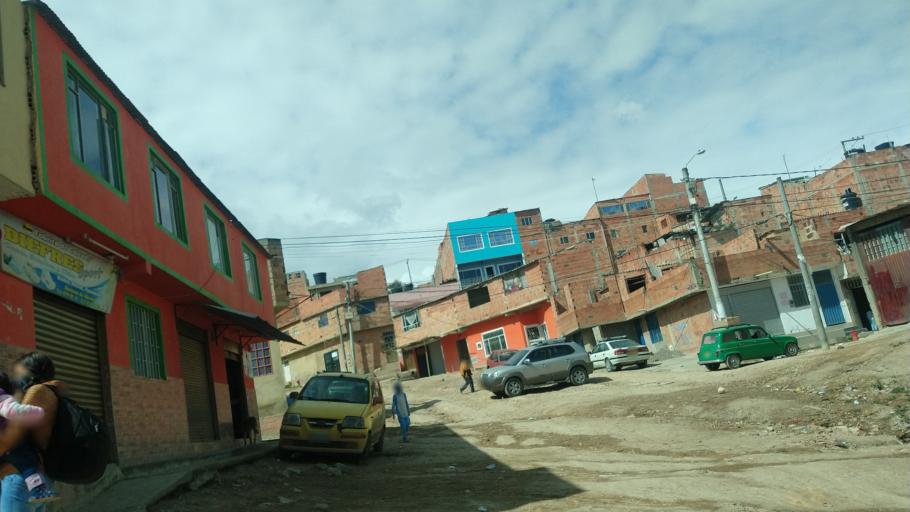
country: CO
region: Cundinamarca
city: Soacha
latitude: 4.5636
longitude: -74.1860
